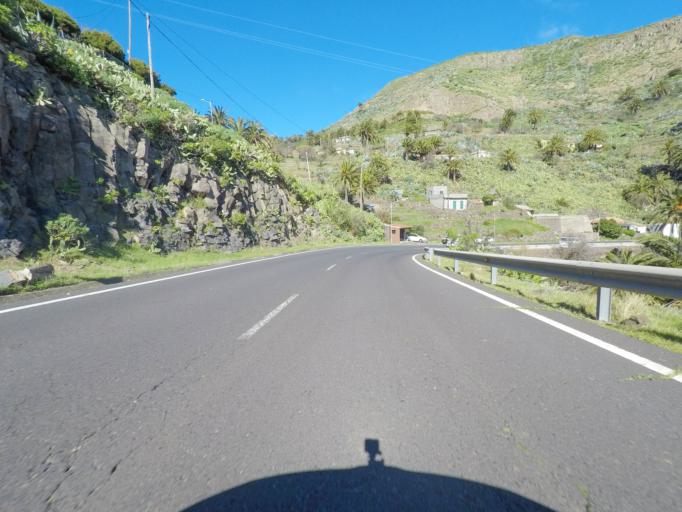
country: ES
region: Canary Islands
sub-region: Provincia de Santa Cruz de Tenerife
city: Alajero
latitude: 28.0936
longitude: -17.2037
